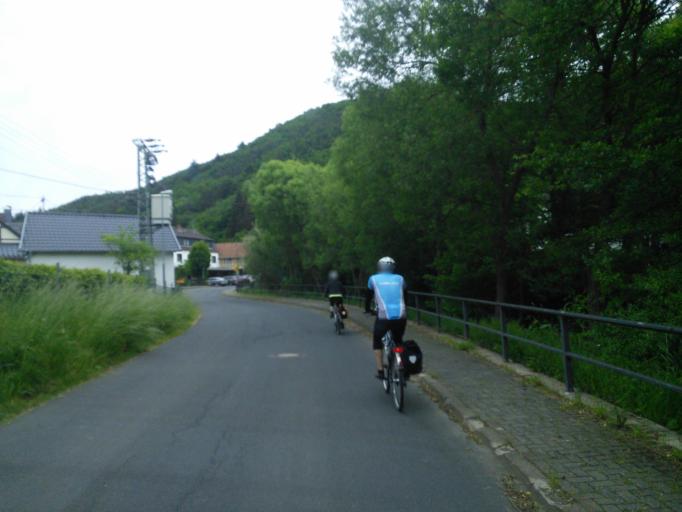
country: DE
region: Rheinland-Pfalz
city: Kirchsahr
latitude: 50.5221
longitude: 6.8991
